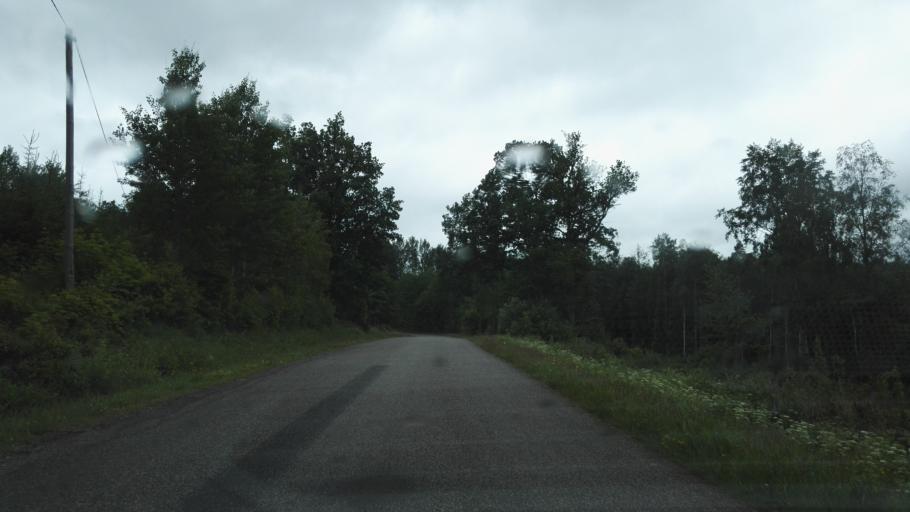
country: SE
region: Joenkoeping
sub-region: Vetlanda Kommun
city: Landsbro
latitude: 57.2516
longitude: 14.8297
